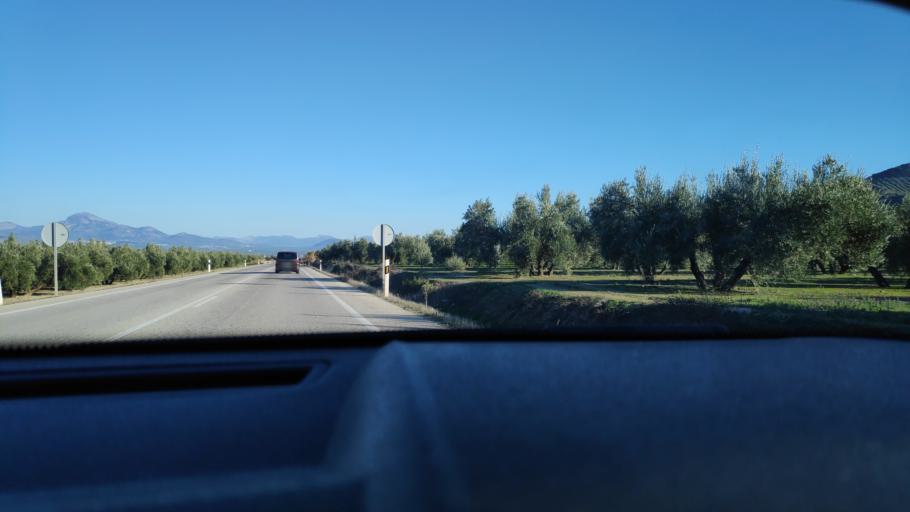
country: ES
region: Andalusia
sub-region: Province of Cordoba
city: Luque
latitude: 37.5646
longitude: -4.2221
